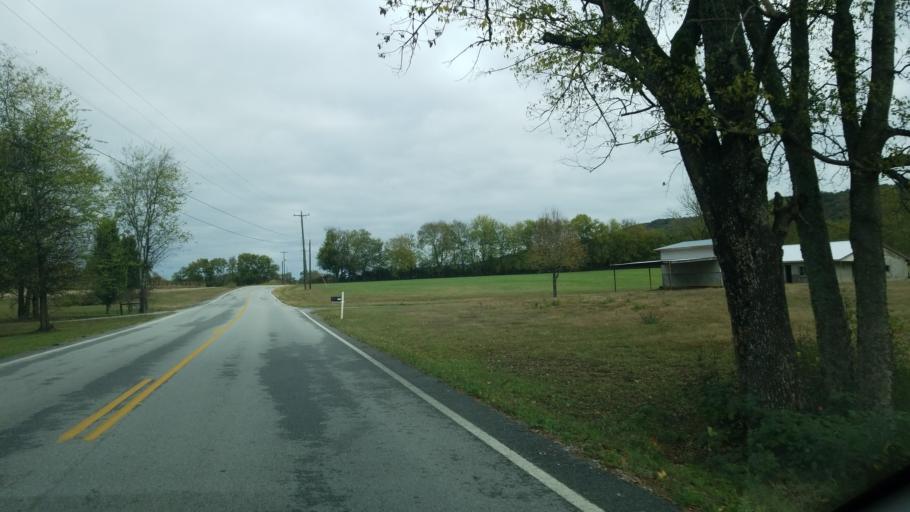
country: US
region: Tennessee
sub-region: Hamilton County
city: Lakesite
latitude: 35.1883
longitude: -85.0213
